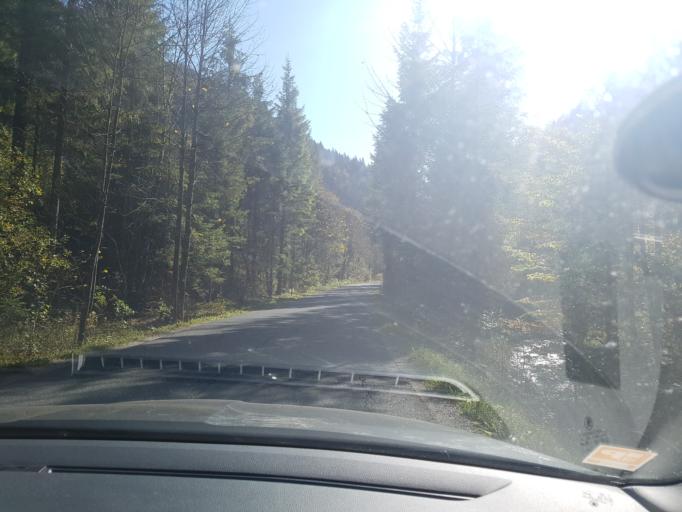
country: AT
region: Tyrol
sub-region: Politischer Bezirk Kitzbuhel
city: Hochfilzen
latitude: 47.5008
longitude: 12.6098
